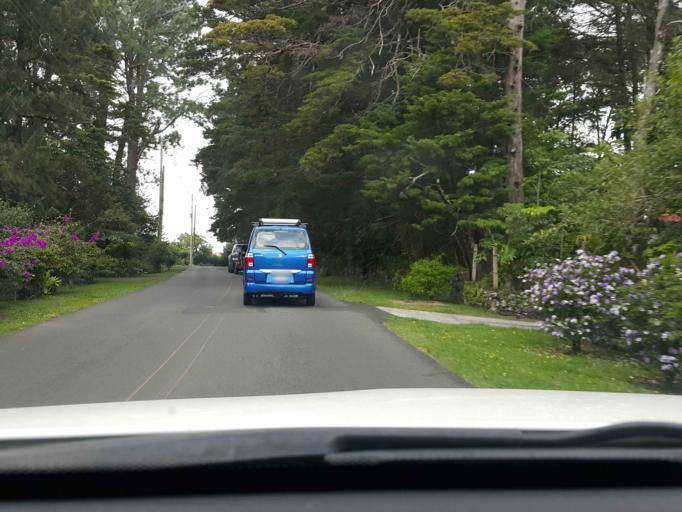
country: CR
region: Heredia
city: San Josecito
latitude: 10.0508
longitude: -84.0874
